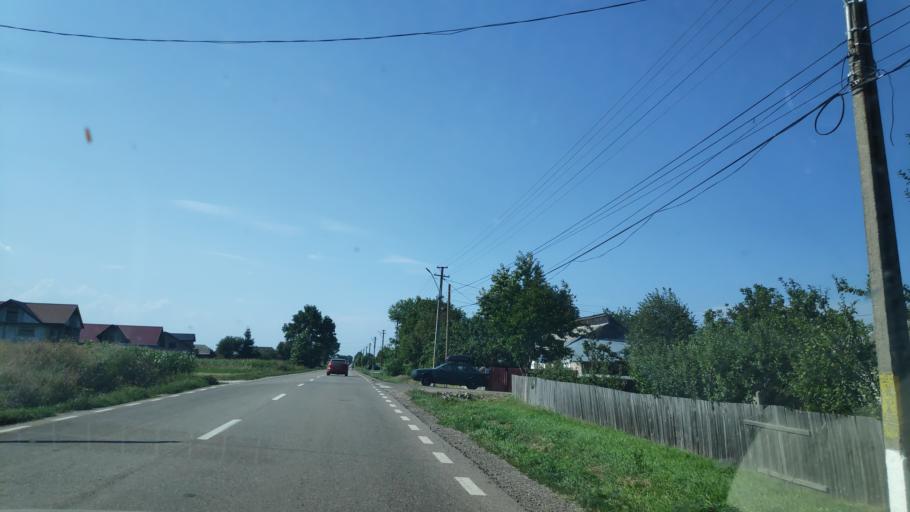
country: RO
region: Suceava
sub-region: Comuna Boroaia
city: Boroaia
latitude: 47.3635
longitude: 26.3377
